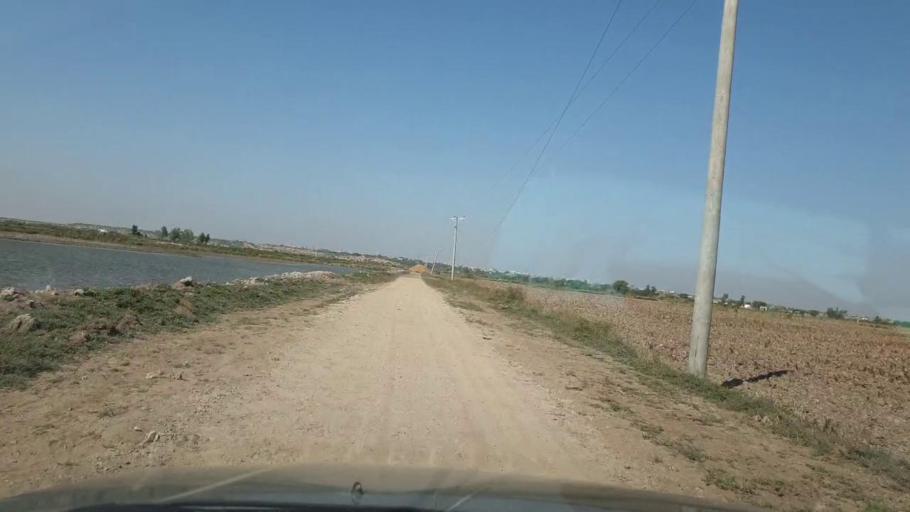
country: PK
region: Sindh
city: Thatta
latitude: 24.7211
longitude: 67.9161
